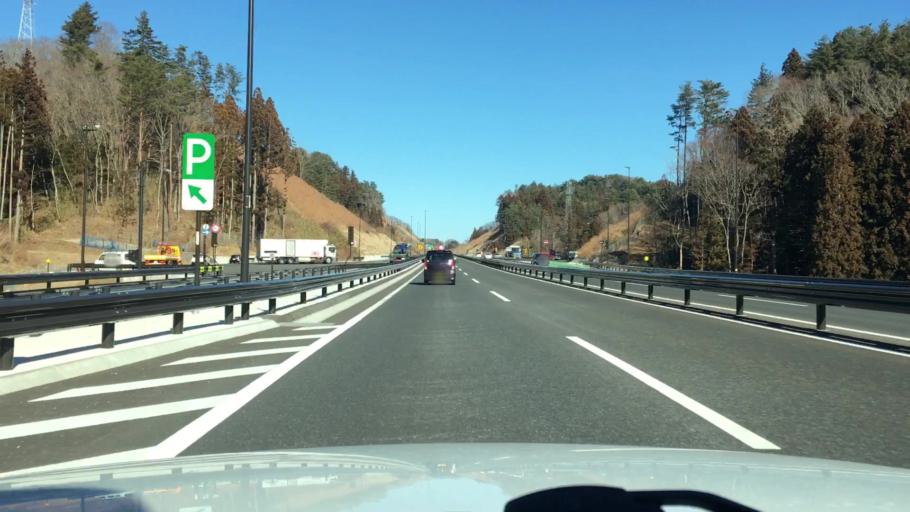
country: JP
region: Iwate
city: Miyako
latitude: 39.5828
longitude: 141.9336
